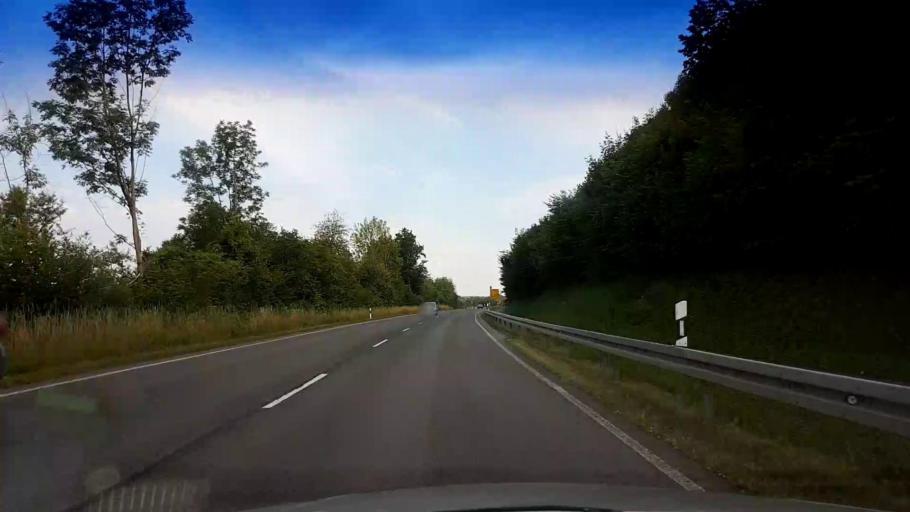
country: DE
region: Bavaria
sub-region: Regierungsbezirk Unterfranken
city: Stettfeld
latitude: 49.9624
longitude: 10.7090
